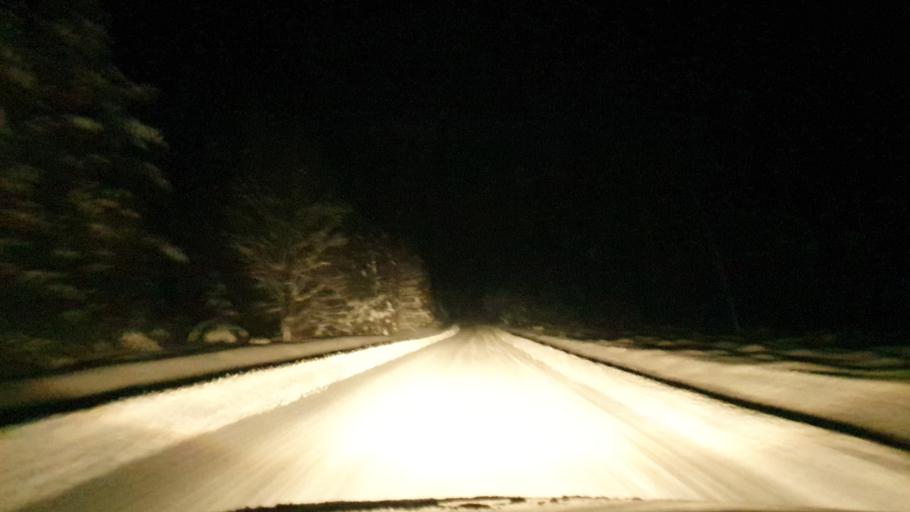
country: EE
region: Vorumaa
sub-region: Antsla vald
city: Vana-Antsla
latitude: 57.9686
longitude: 26.7136
